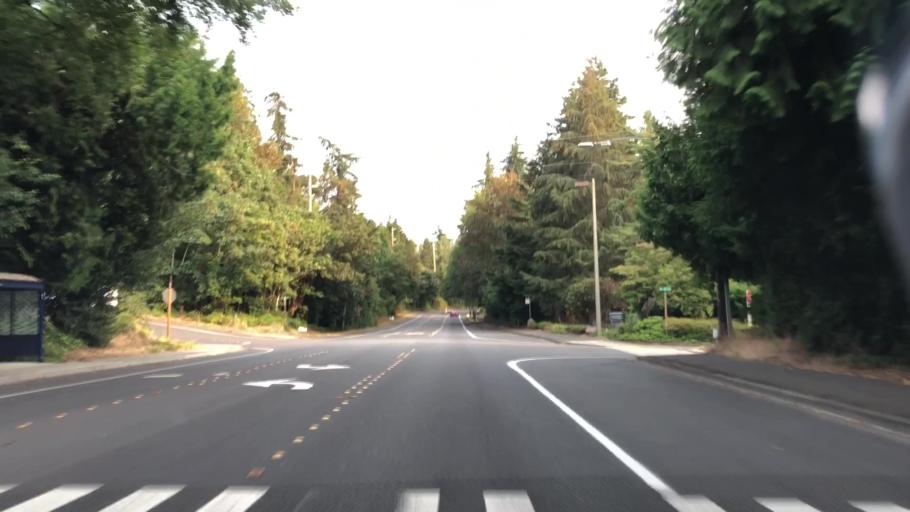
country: US
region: Washington
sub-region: King County
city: Mercer Island
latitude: 47.5621
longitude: -122.2225
